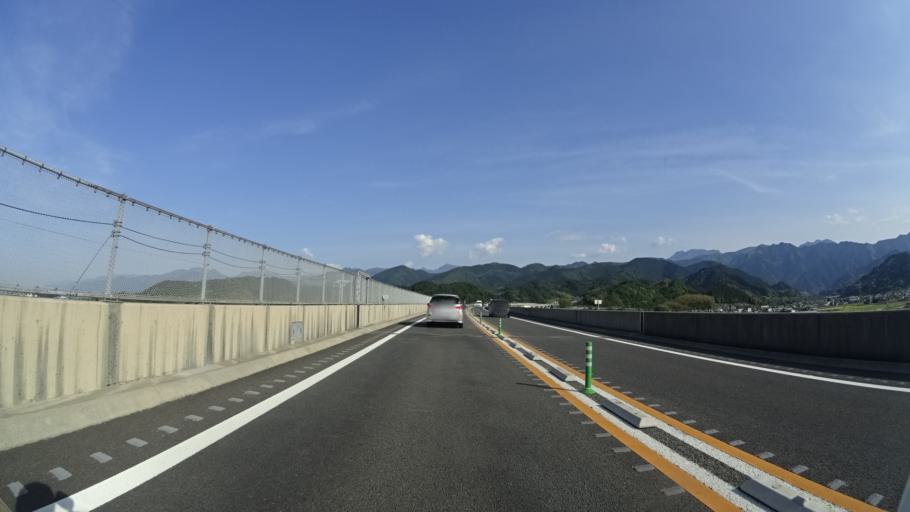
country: JP
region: Ehime
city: Saijo
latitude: 33.8933
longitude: 133.0831
